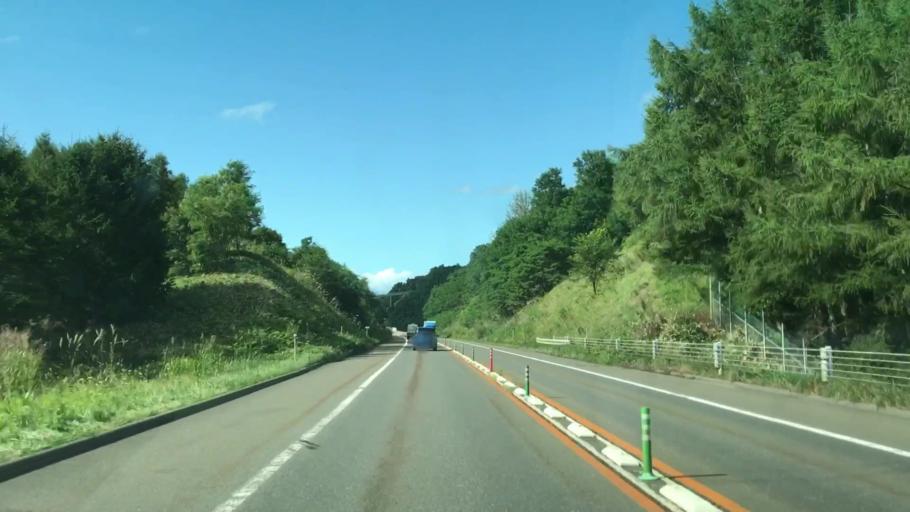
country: JP
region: Hokkaido
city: Date
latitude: 42.4550
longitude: 140.9128
